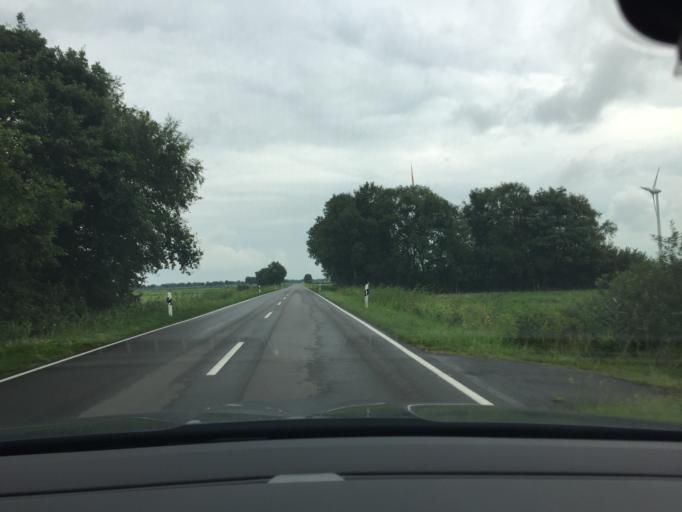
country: DE
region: Lower Saxony
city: Jemgum
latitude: 53.3614
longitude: 7.3531
